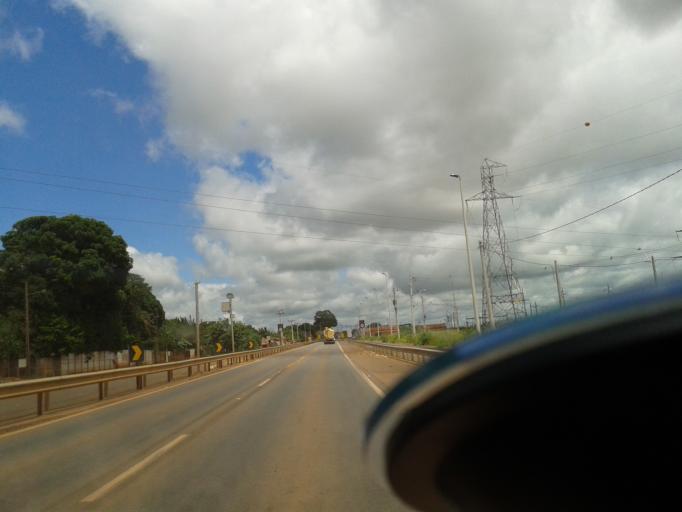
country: BR
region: Goias
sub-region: Itaberai
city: Itaberai
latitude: -16.0516
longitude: -49.7861
